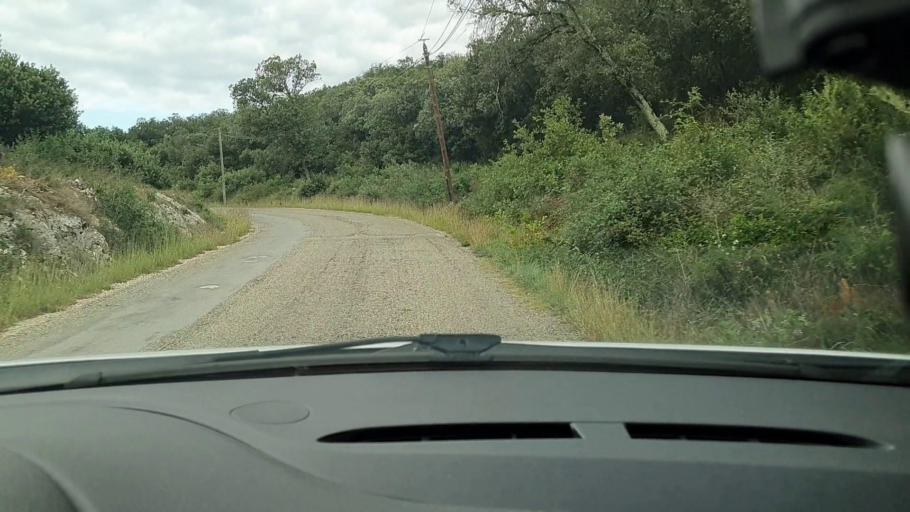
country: FR
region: Languedoc-Roussillon
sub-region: Departement du Gard
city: Montaren-et-Saint-Mediers
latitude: 44.0624
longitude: 4.3162
